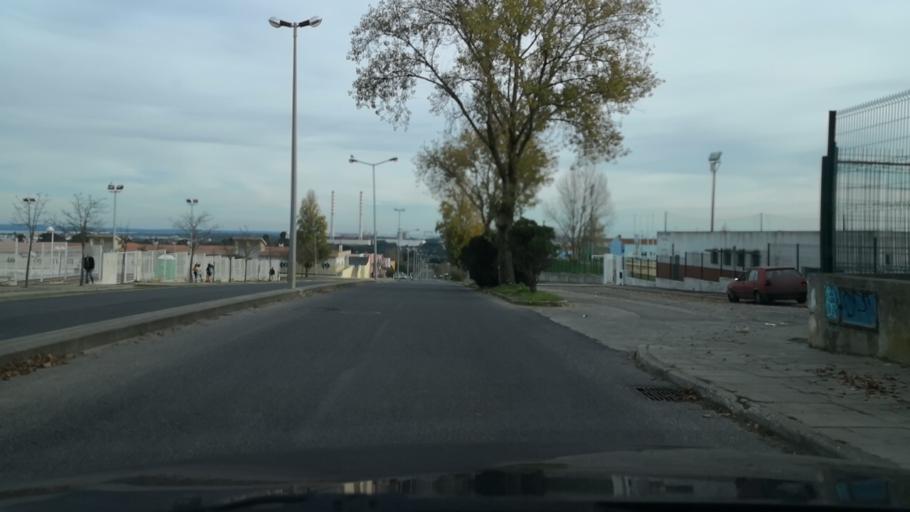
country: PT
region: Setubal
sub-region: Setubal
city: Setubal
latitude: 38.5208
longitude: -8.8717
